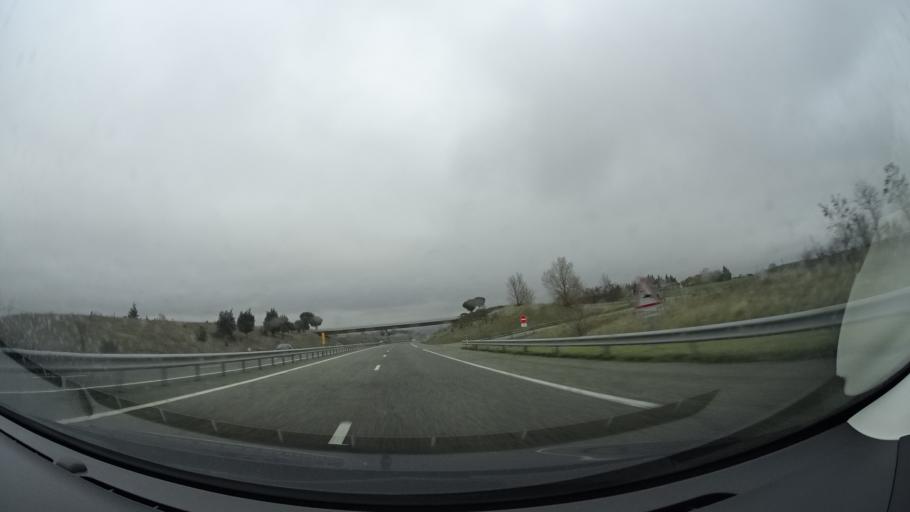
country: FR
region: Midi-Pyrenees
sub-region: Departement de la Haute-Garonne
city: Villenouvelle
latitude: 43.4004
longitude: 1.6408
